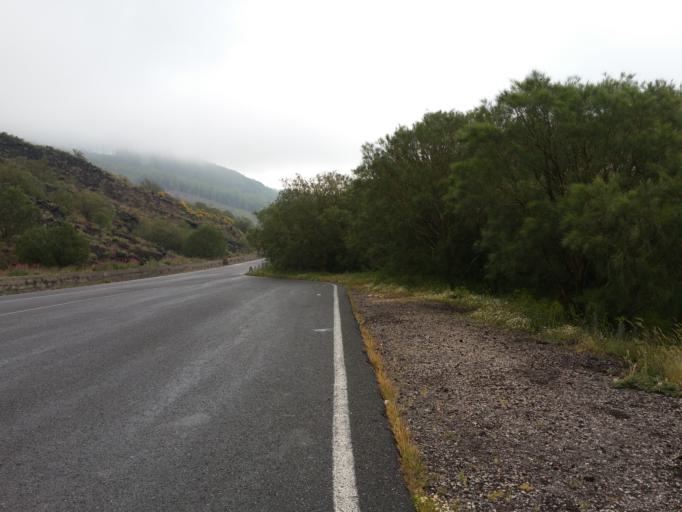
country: IT
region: Sicily
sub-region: Catania
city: Nicolosi
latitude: 37.6659
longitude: 15.0268
